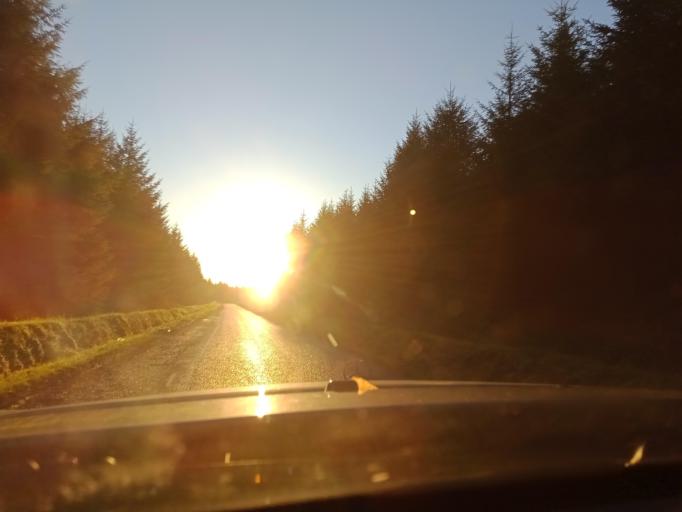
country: IE
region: Munster
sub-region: Waterford
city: Waterford
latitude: 52.3717
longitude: -7.1042
